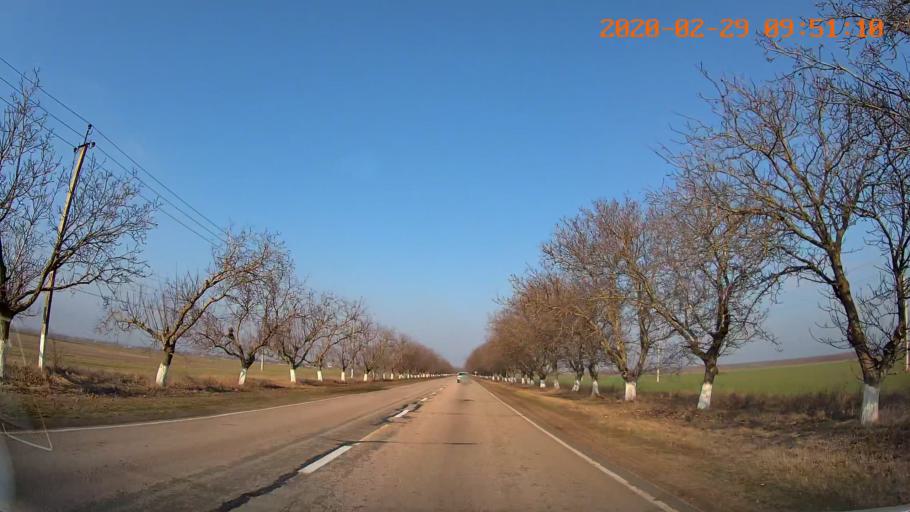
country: MD
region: Telenesti
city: Slobozia
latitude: 46.7064
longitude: 29.7437
